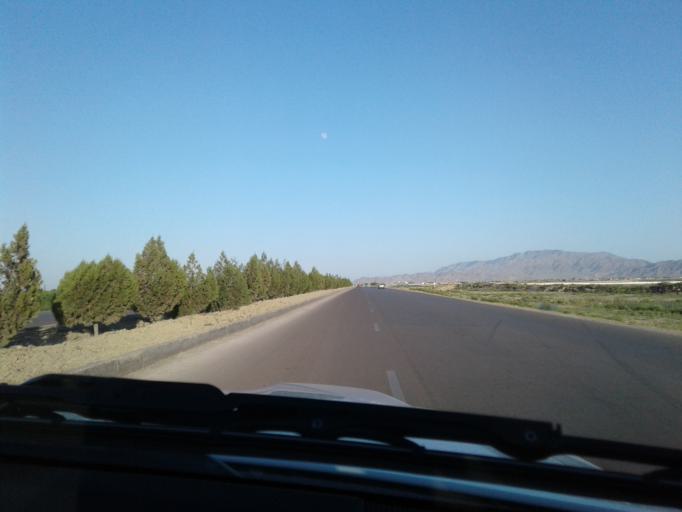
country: TM
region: Ahal
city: Baharly
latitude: 38.3370
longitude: 57.5695
